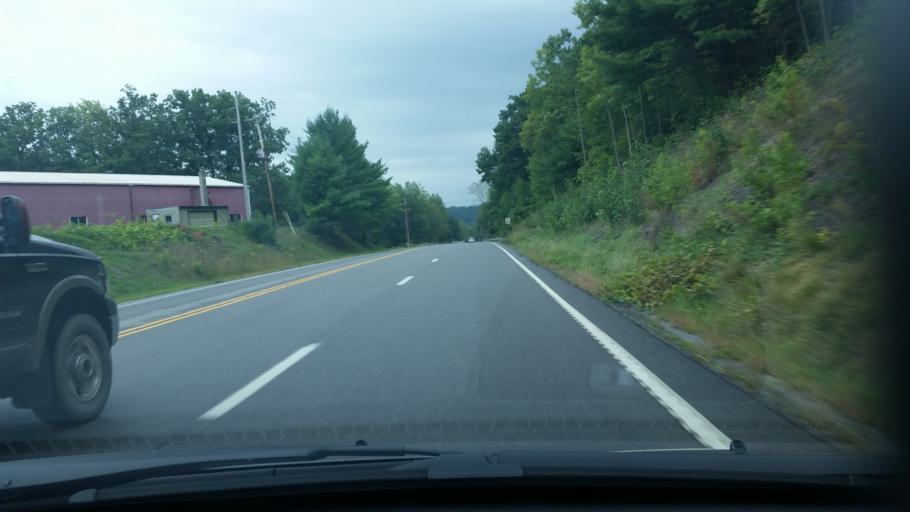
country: US
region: Pennsylvania
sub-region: Clearfield County
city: Shiloh
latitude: 41.0713
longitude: -78.3094
